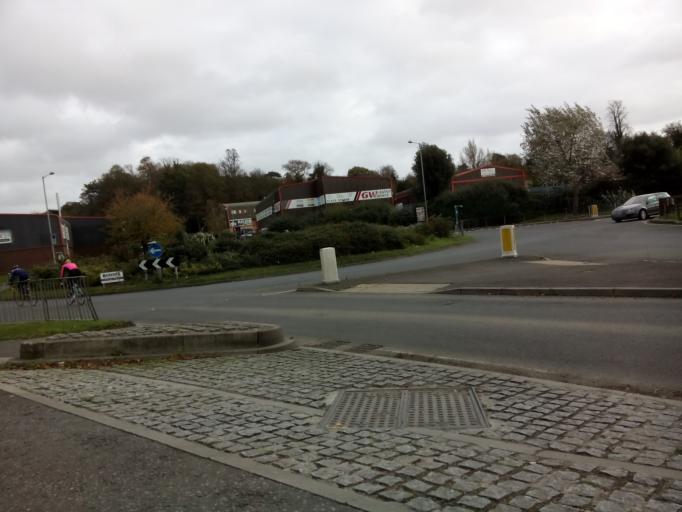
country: GB
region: England
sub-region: Suffolk
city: Ipswich
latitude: 52.0486
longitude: 1.1662
